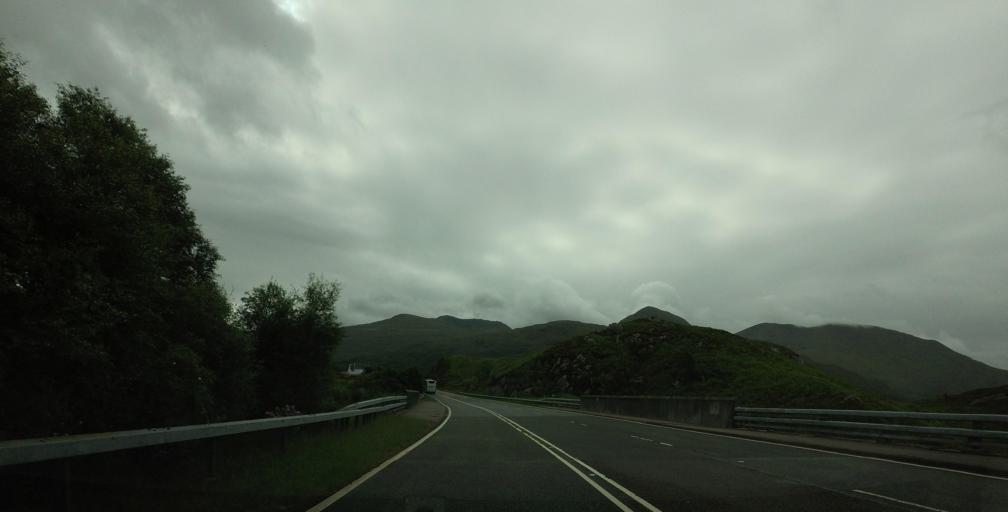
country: GB
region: Scotland
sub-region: Argyll and Bute
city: Isle Of Mull
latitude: 56.8833
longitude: -5.6983
